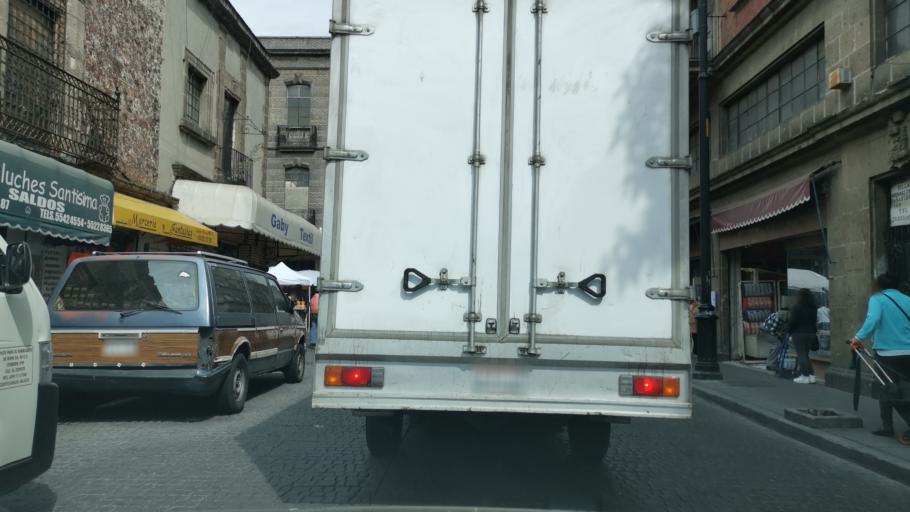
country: MX
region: Mexico City
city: Mexico City
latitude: 19.4291
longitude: -99.1285
